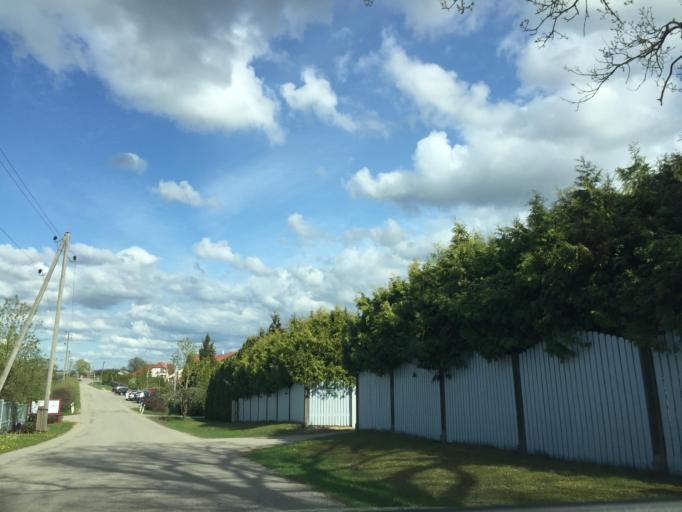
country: LV
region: Sigulda
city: Sigulda
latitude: 57.1321
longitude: 24.8520
